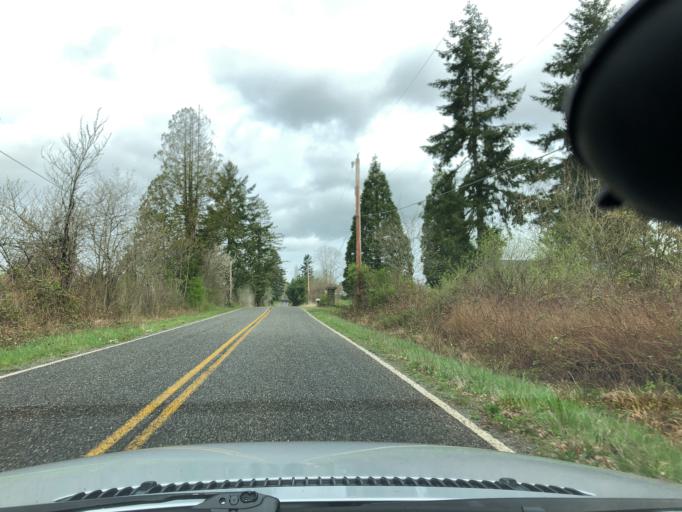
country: US
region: Washington
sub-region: Whatcom County
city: Blaine
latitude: 48.9729
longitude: -122.7039
